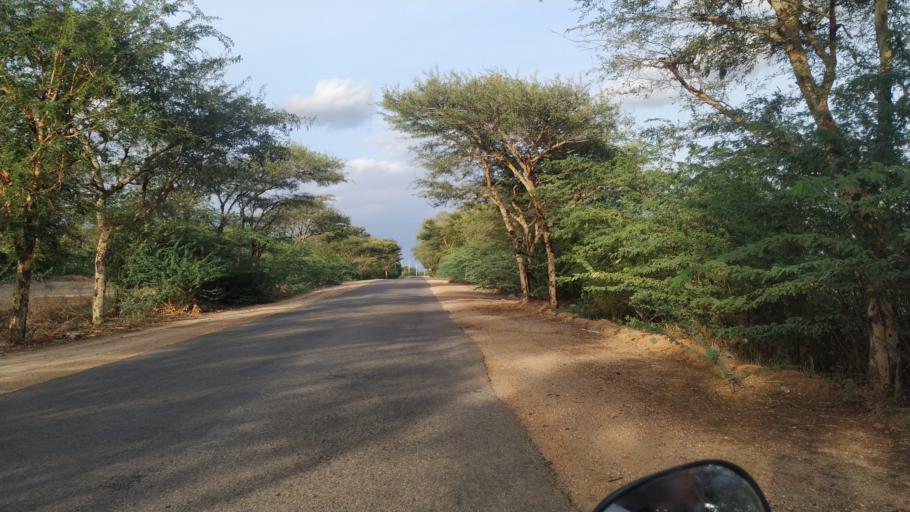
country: MM
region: Magway
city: Pakokku
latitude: 21.3560
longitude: 94.9063
